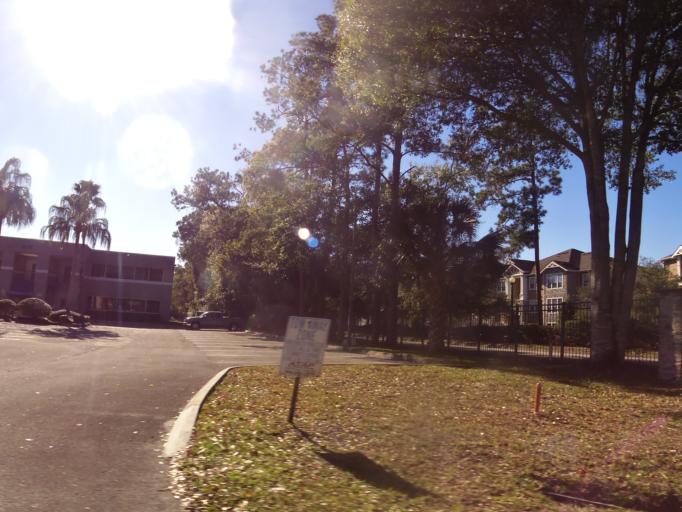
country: US
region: Florida
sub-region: Duval County
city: Jacksonville
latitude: 30.2547
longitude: -81.5953
